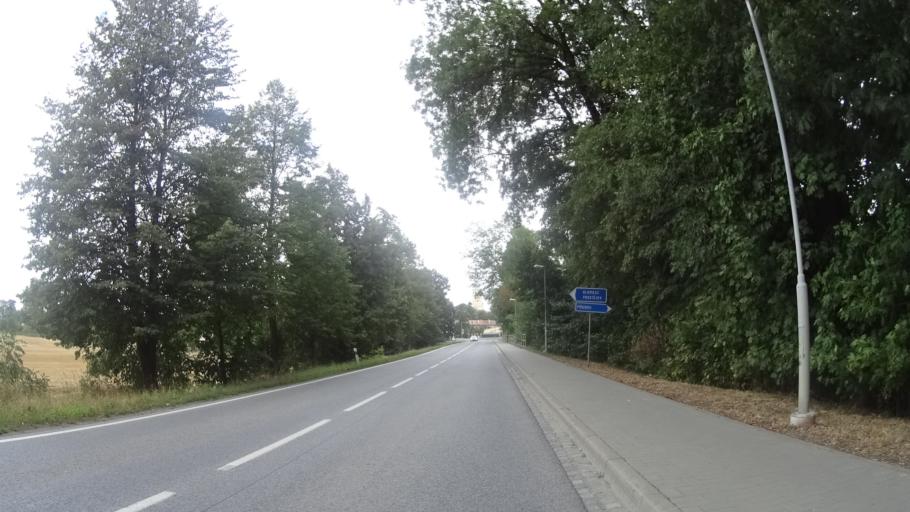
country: CZ
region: Olomoucky
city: Tovacov
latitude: 49.4246
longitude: 17.2912
